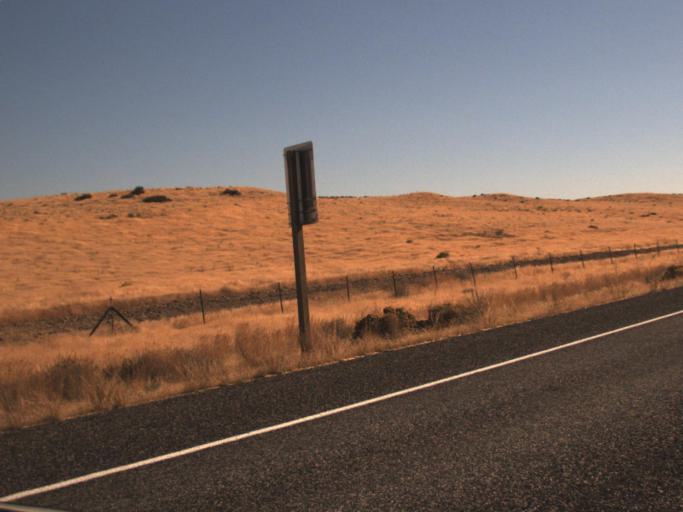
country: US
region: Washington
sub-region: Benton County
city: Benton City
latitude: 46.4499
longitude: -119.5051
